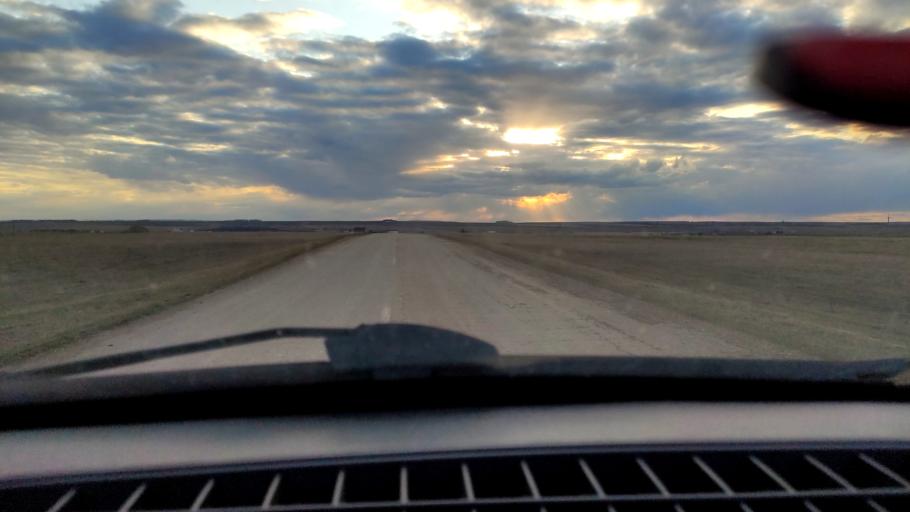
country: RU
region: Bashkortostan
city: Tolbazy
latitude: 54.0141
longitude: 55.5498
